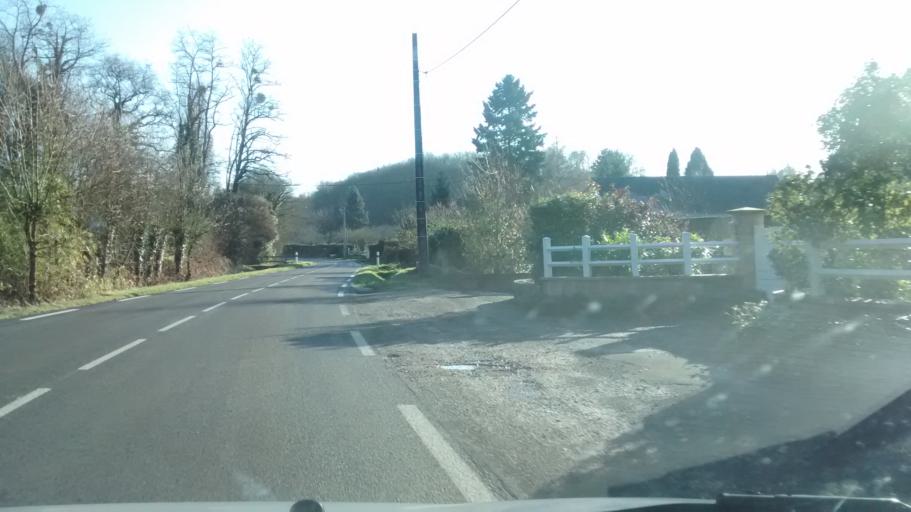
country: FR
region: Centre
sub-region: Departement d'Indre-et-Loire
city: Reugny
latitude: 47.4840
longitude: 0.8677
